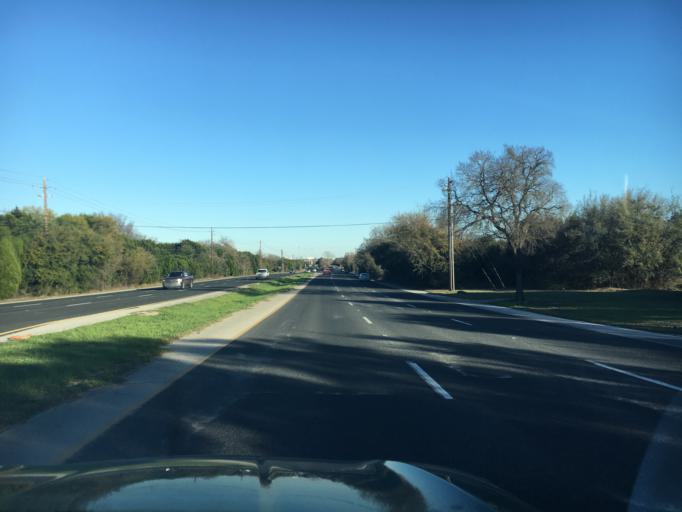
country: US
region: Texas
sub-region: Travis County
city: Barton Creek
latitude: 30.2433
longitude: -97.8403
